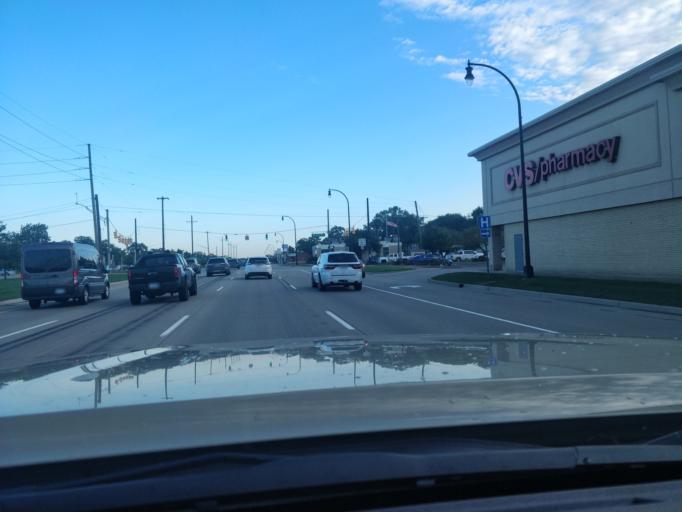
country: US
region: Michigan
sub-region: Wayne County
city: Southgate
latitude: 42.2129
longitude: -83.1806
